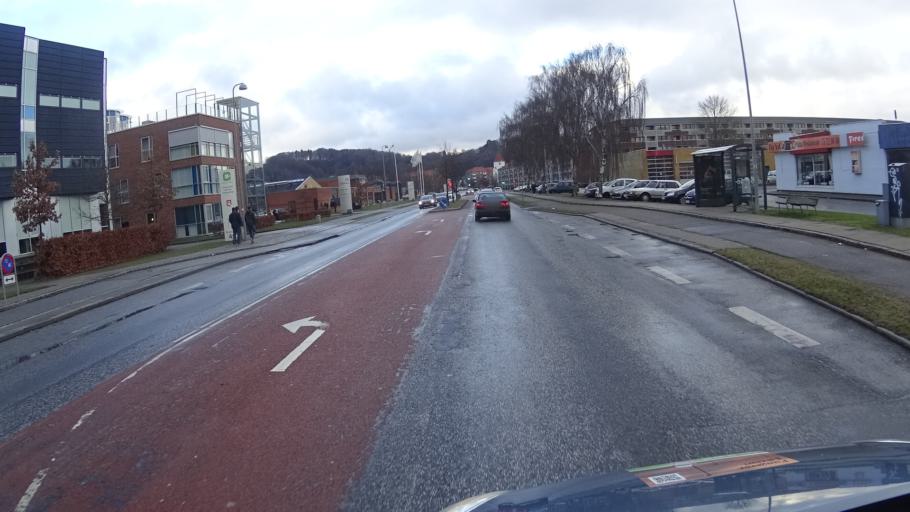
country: DK
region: South Denmark
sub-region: Vejle Kommune
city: Vejle
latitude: 55.7104
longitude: 9.5229
